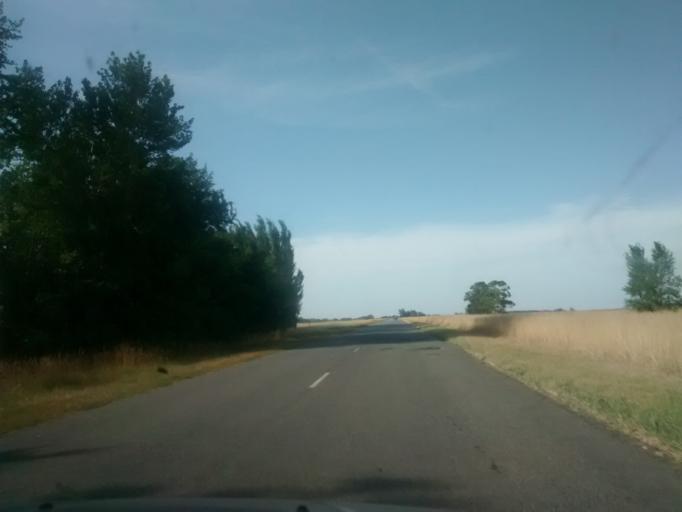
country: AR
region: Buenos Aires
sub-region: Partido de Ayacucho
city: Ayacucho
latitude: -37.4776
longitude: -58.4787
